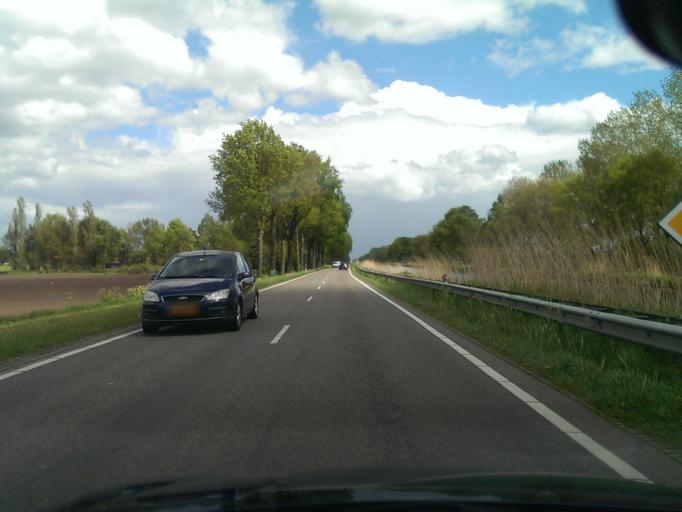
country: NL
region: Limburg
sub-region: Gemeente Nederweert
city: Nederweert
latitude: 51.2946
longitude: 5.8116
